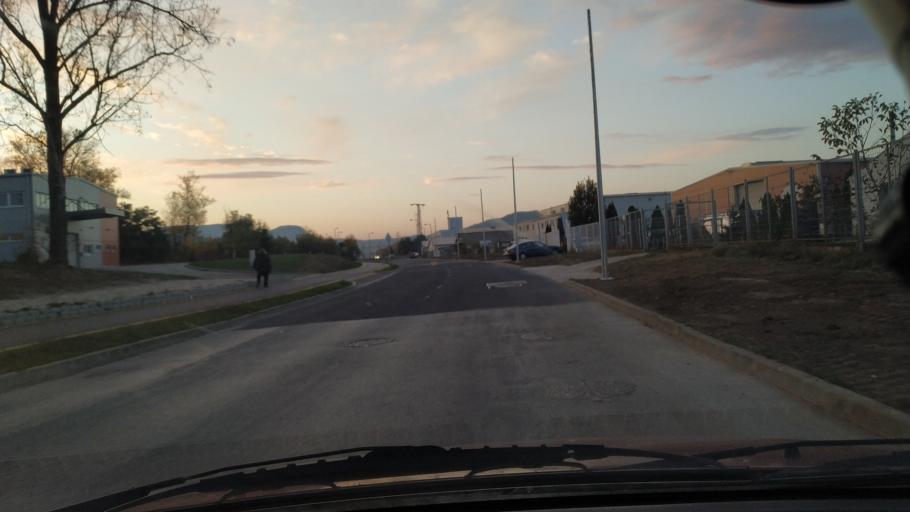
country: HU
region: Komarom-Esztergom
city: Esztergom
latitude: 47.7756
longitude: 18.7498
